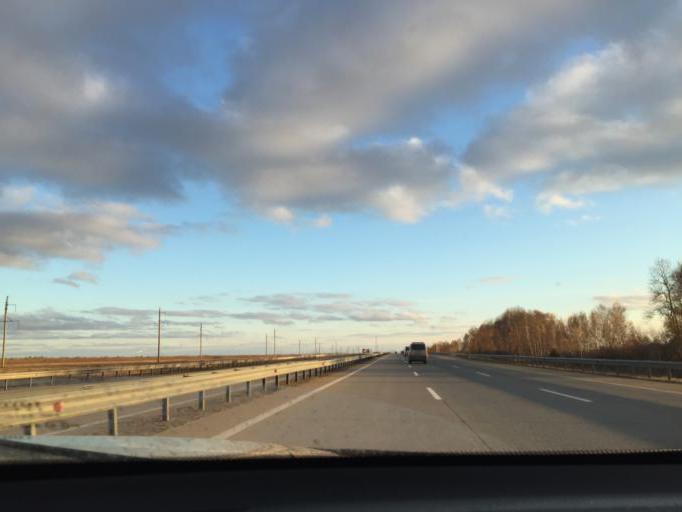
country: KZ
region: Astana Qalasy
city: Astana
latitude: 51.3190
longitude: 71.3485
